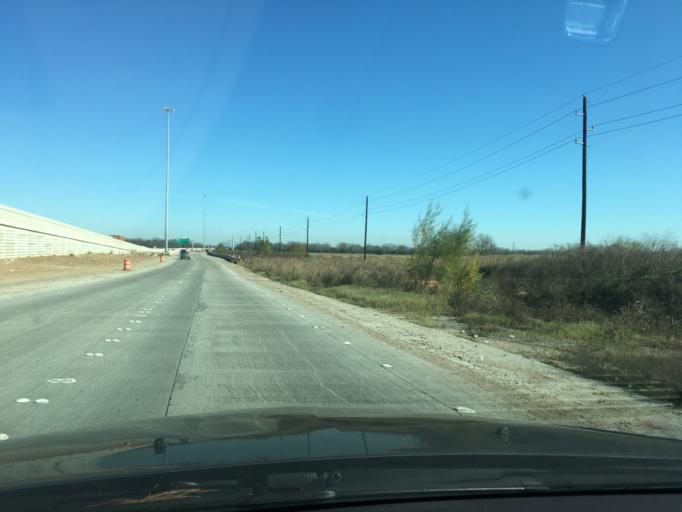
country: US
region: Texas
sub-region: Fort Bend County
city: Richmond
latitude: 29.5477
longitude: -95.7432
